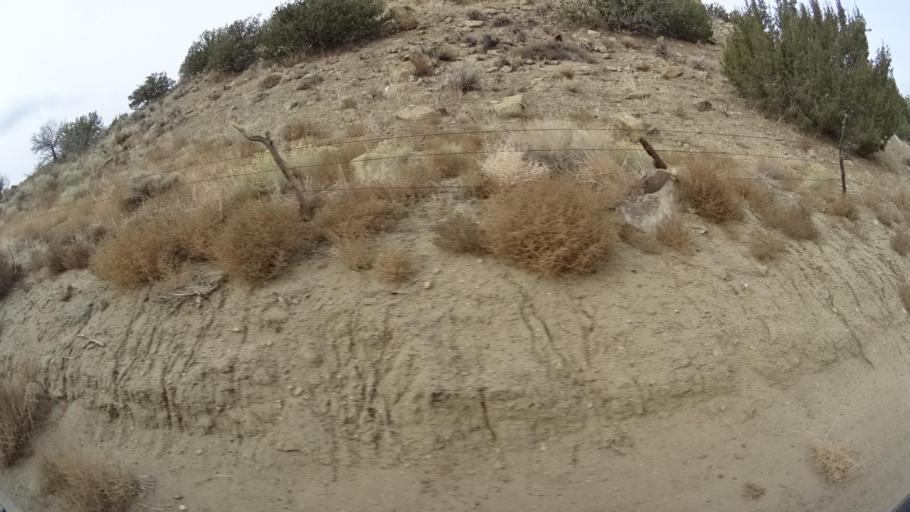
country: US
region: California
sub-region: Kern County
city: Tehachapi
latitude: 35.1273
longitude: -118.3254
